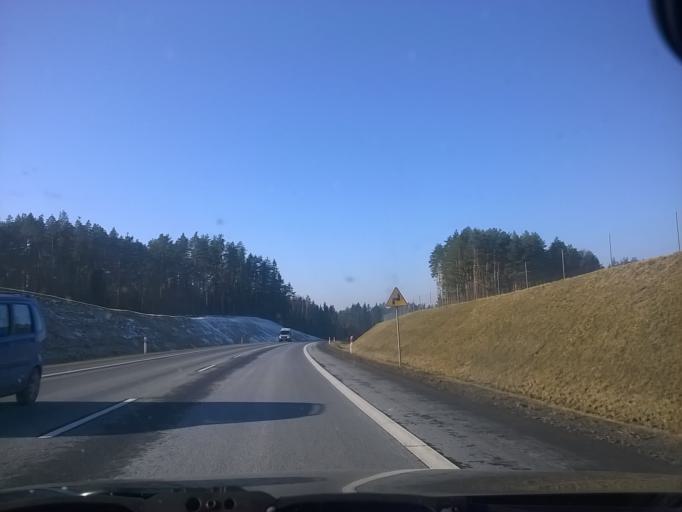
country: PL
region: Warmian-Masurian Voivodeship
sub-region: Powiat olsztynski
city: Barczewo
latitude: 53.8290
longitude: 20.7825
